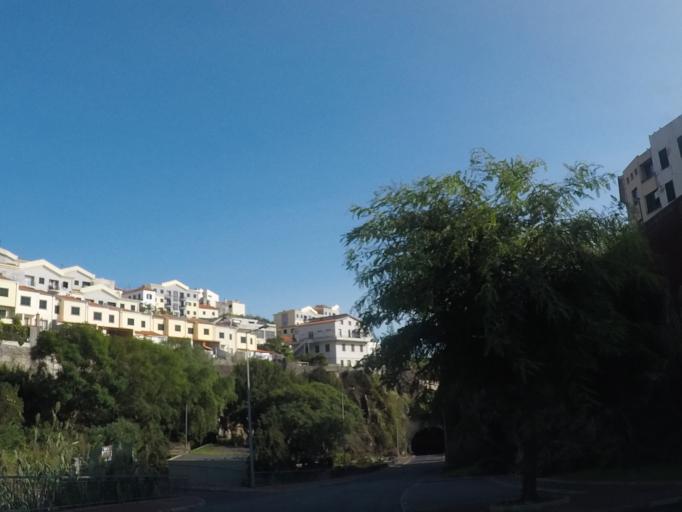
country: PT
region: Madeira
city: Camara de Lobos
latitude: 32.6520
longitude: -16.9827
